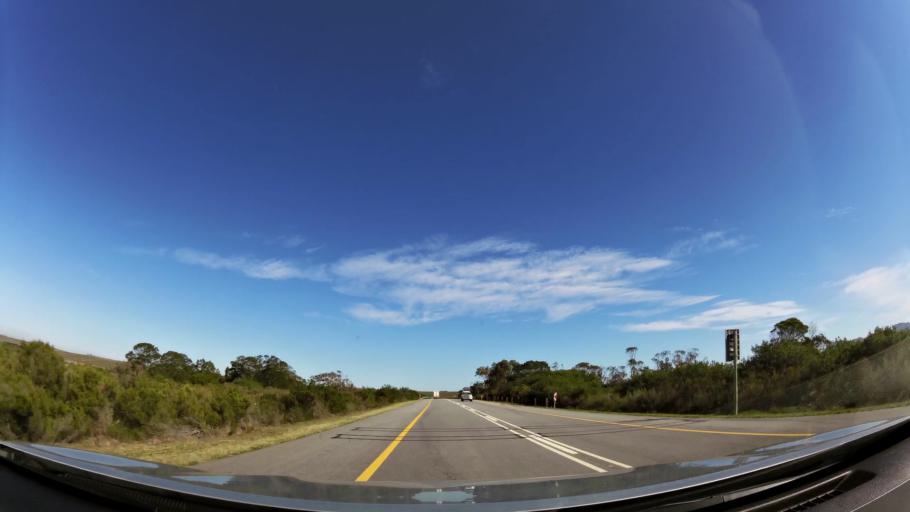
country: ZA
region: Eastern Cape
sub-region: Cacadu District Municipality
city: Kruisfontein
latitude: -34.0345
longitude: 24.5933
